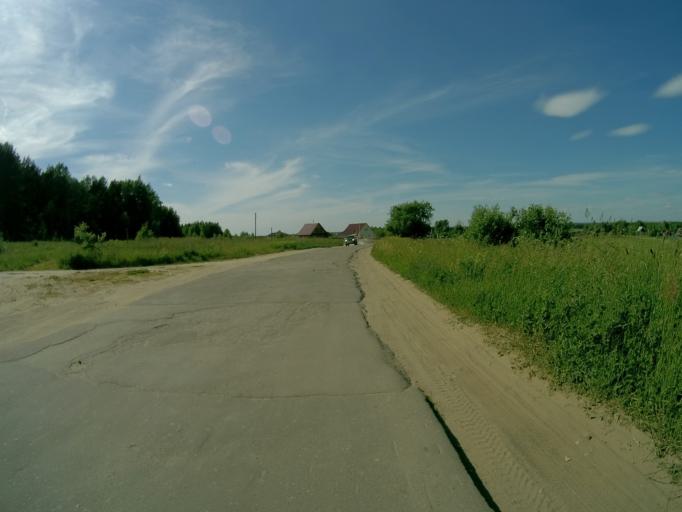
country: RU
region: Vladimir
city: Raduzhnyy
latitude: 56.0180
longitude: 40.3360
